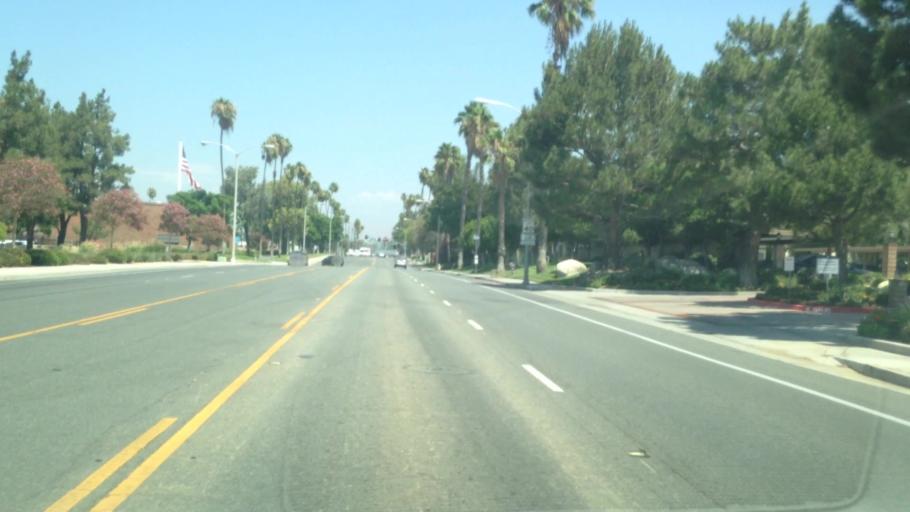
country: US
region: California
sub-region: Riverside County
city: Riverside
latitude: 33.9208
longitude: -117.4136
